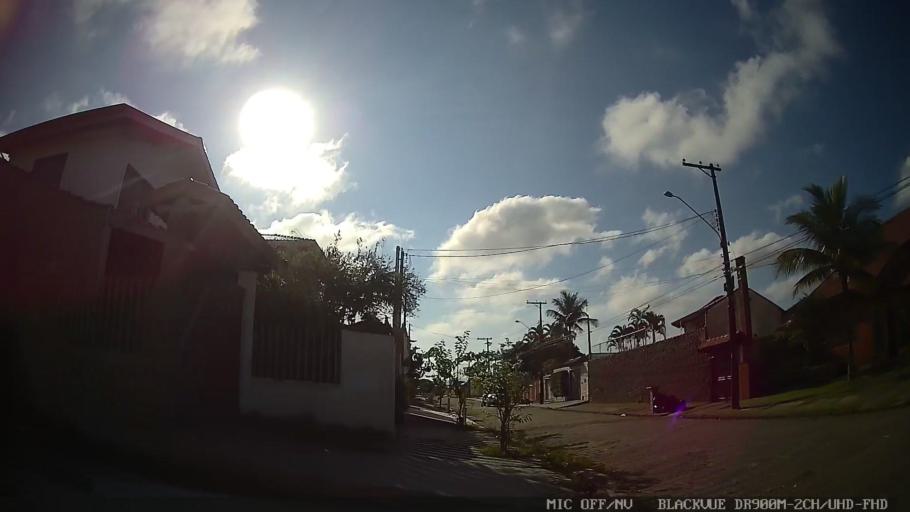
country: BR
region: Sao Paulo
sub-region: Peruibe
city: Peruibe
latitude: -24.2887
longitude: -46.9627
